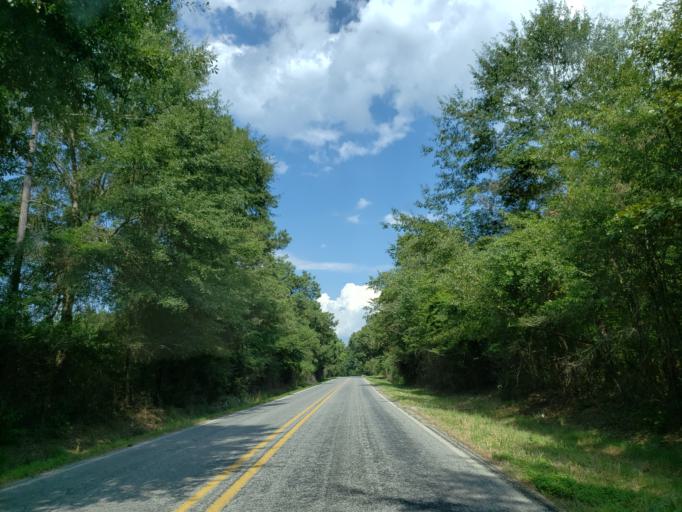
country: US
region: Mississippi
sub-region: Covington County
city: Collins
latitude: 31.6199
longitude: -89.3824
